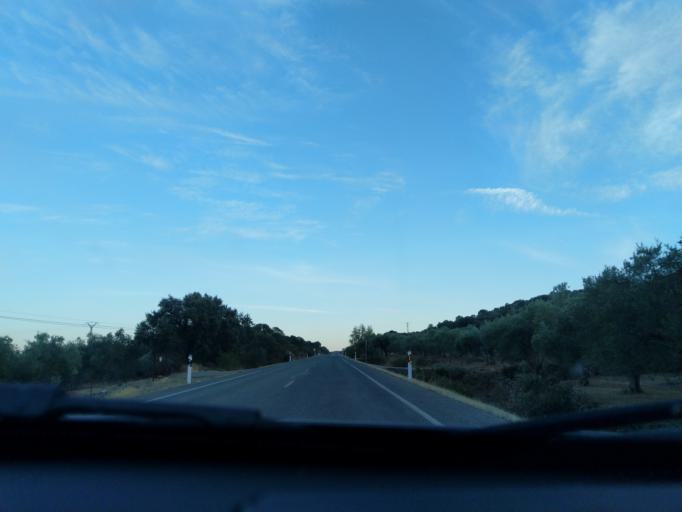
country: ES
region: Extremadura
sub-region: Provincia de Badajoz
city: Reina
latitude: 38.1812
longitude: -5.9300
